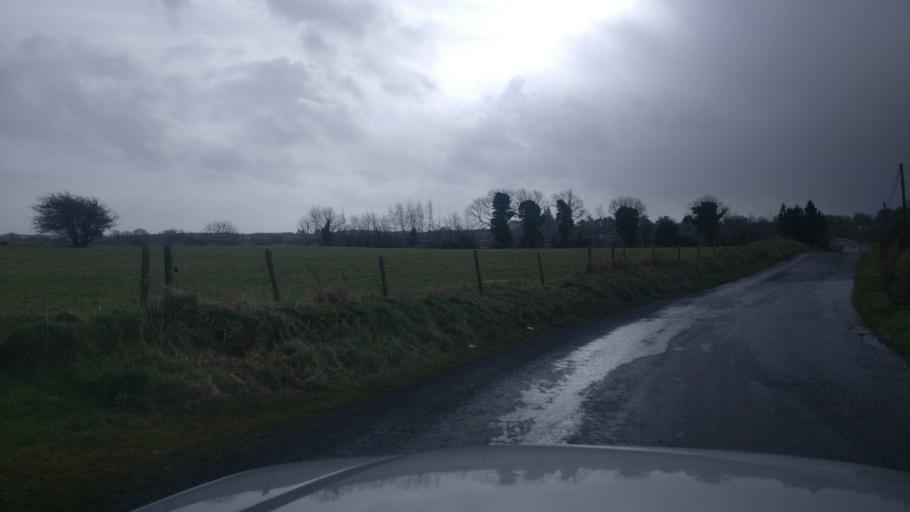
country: IE
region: Connaught
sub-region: County Galway
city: Loughrea
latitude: 53.2905
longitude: -8.4760
